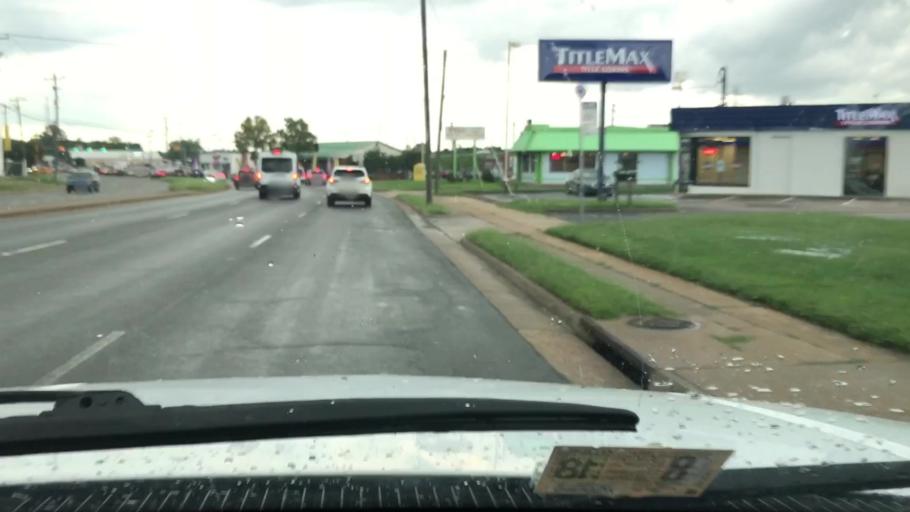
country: US
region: Virginia
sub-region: Henrico County
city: Dumbarton
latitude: 37.6115
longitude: -77.4961
